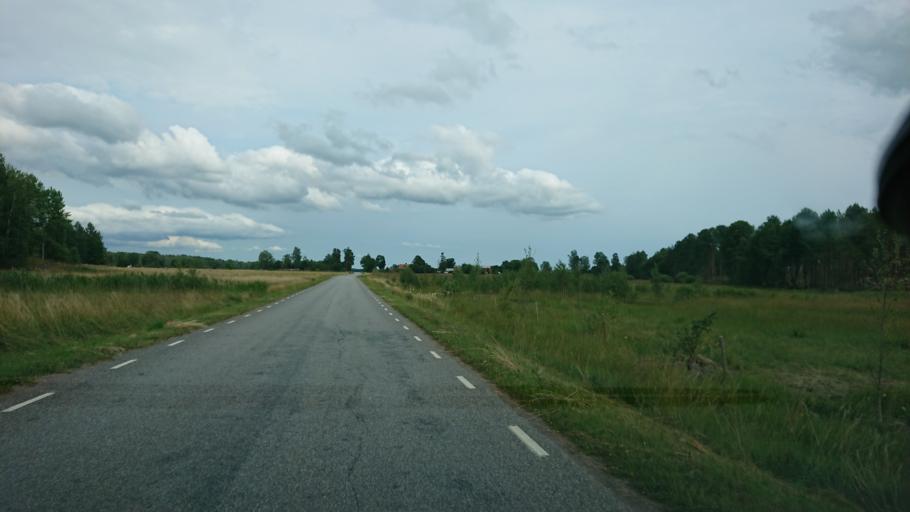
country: SE
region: Uppsala
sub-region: Osthammars Kommun
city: Bjorklinge
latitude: 59.9990
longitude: 17.4782
